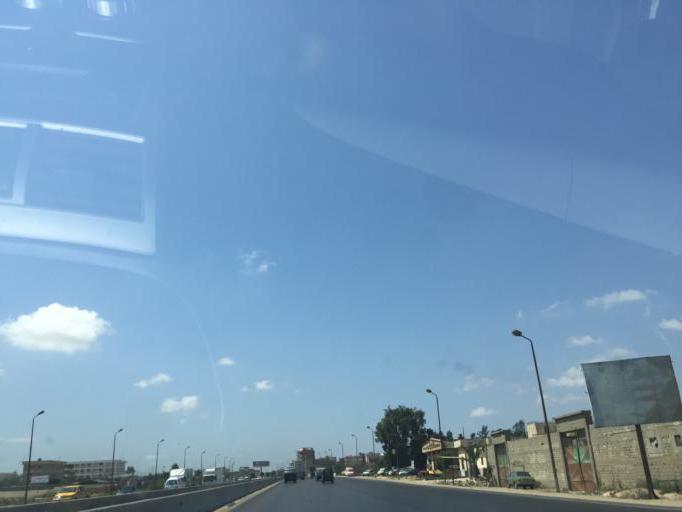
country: EG
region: Alexandria
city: Alexandria
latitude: 31.0000
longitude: 29.8075
